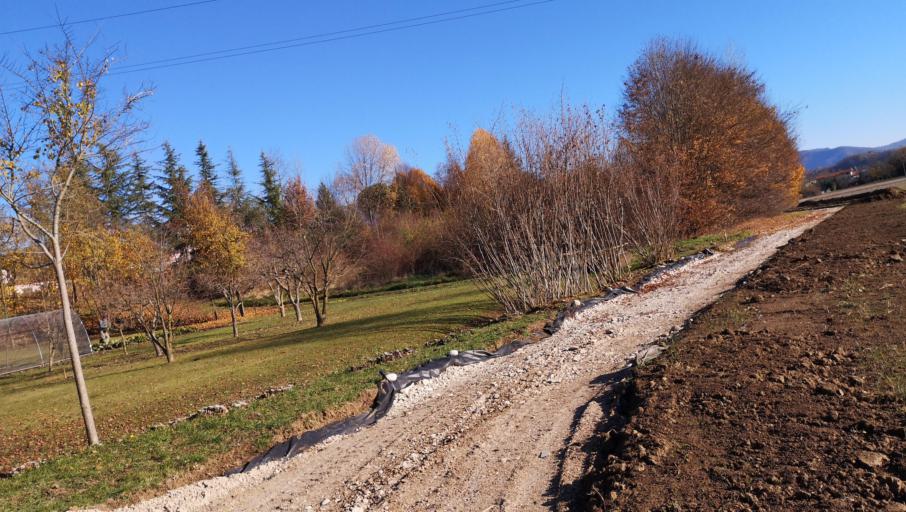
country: IT
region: Friuli Venezia Giulia
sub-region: Provincia di Udine
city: Magnano in Riviera
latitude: 46.2102
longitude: 13.1979
